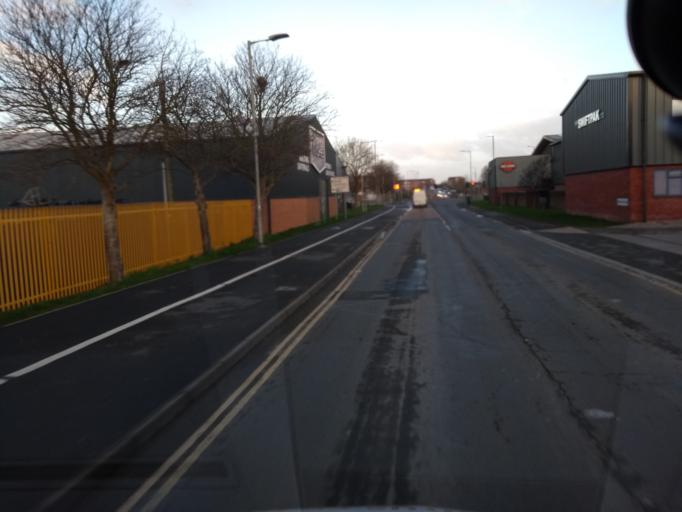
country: GB
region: England
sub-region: Somerset
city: Bridgwater
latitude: 51.1361
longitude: -2.9984
